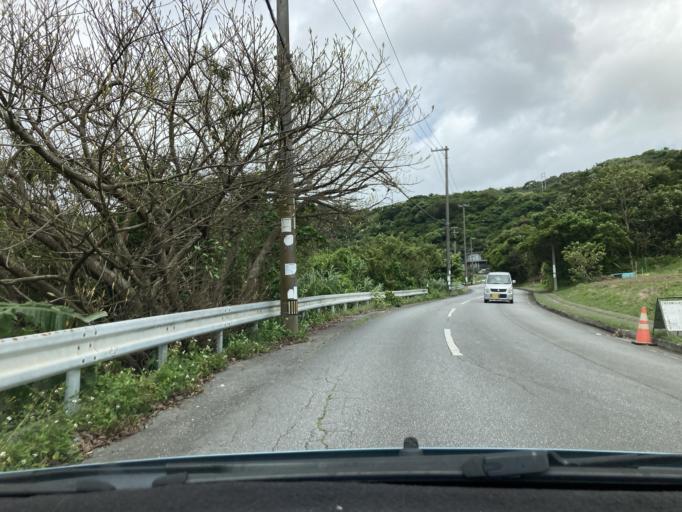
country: JP
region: Okinawa
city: Ginowan
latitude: 26.2293
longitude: 127.7495
